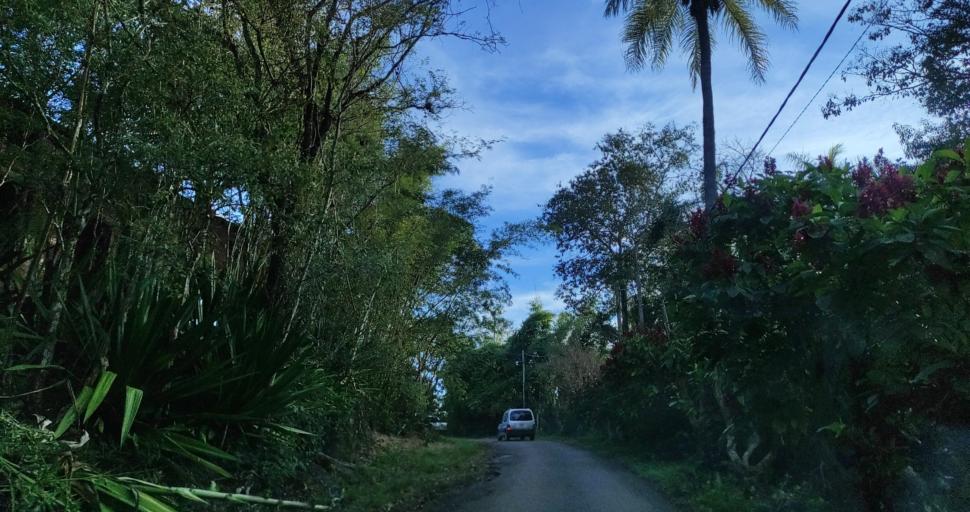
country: AR
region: Misiones
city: Puerto Rico
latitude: -26.7917
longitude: -55.0164
